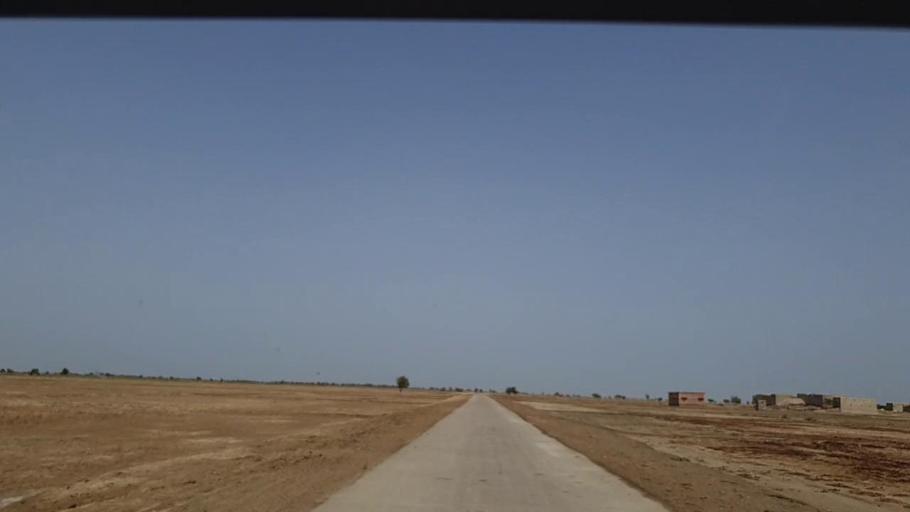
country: PK
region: Sindh
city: Johi
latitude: 26.7707
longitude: 67.6455
